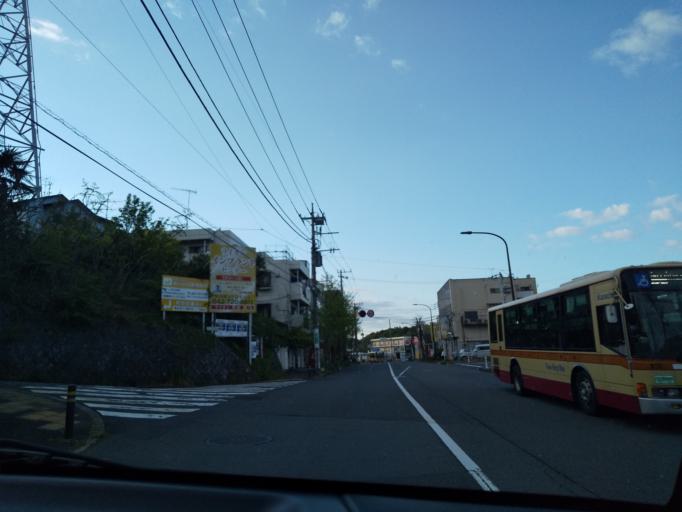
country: JP
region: Tokyo
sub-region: Machida-shi
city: Machida
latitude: 35.5547
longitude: 139.4277
